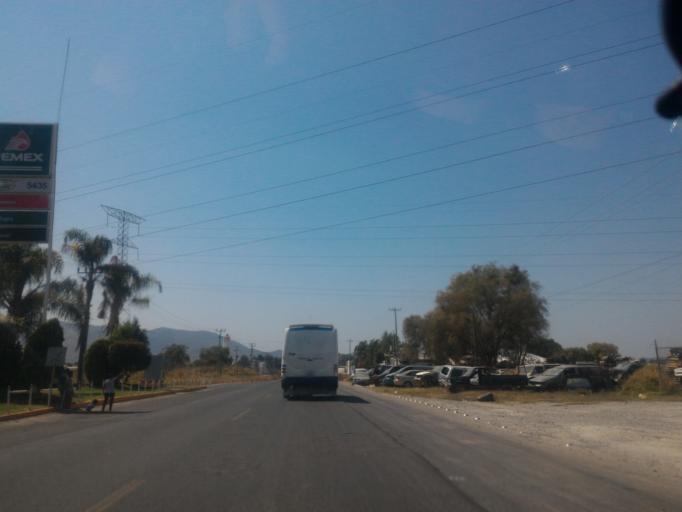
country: MX
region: Jalisco
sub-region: San Pedro Tlaquepaque
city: Paseo del Prado
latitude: 20.5637
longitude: -103.4132
